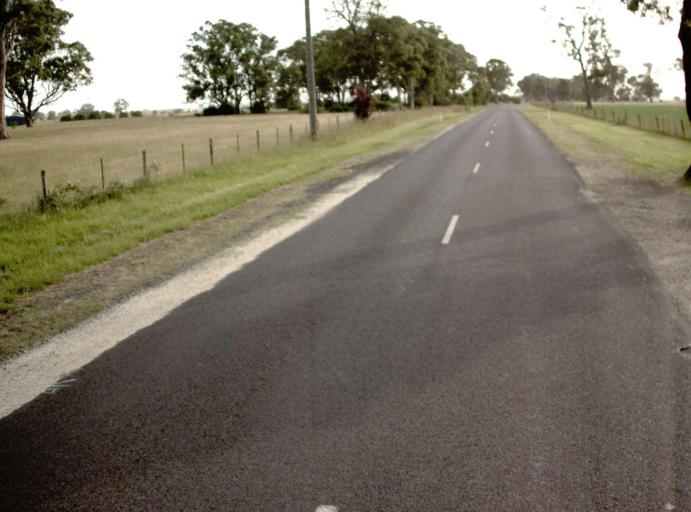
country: AU
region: Victoria
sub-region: Wellington
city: Sale
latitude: -37.8562
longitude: 147.0420
